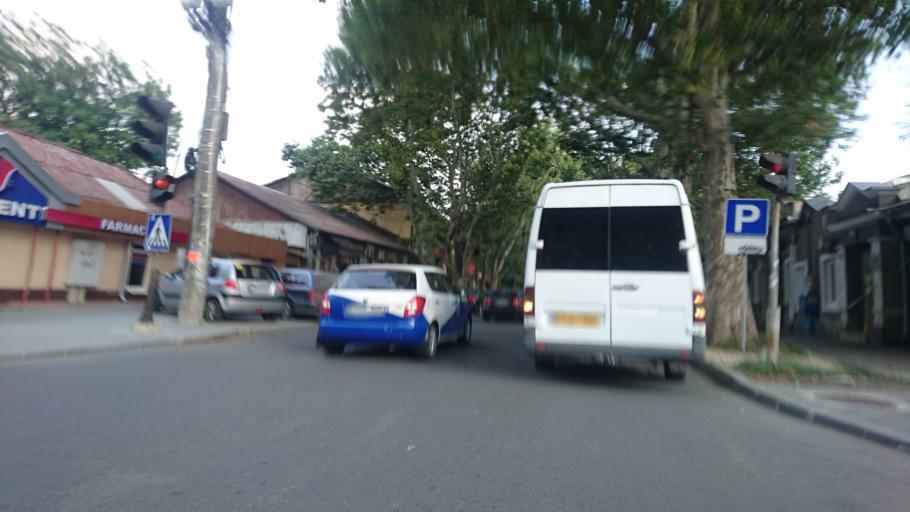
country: MD
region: Chisinau
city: Chisinau
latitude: 47.0188
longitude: 28.8352
